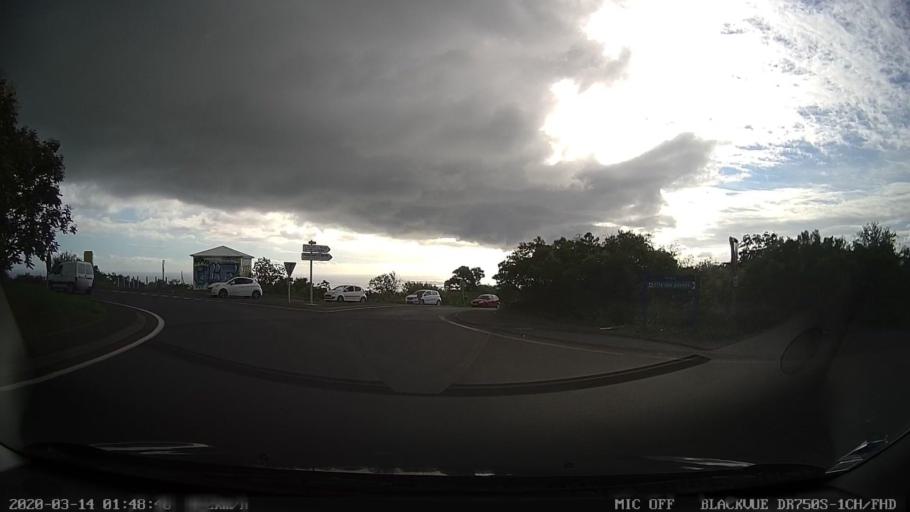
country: RE
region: Reunion
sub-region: Reunion
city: Saint-Paul
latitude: -21.0672
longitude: 55.2469
